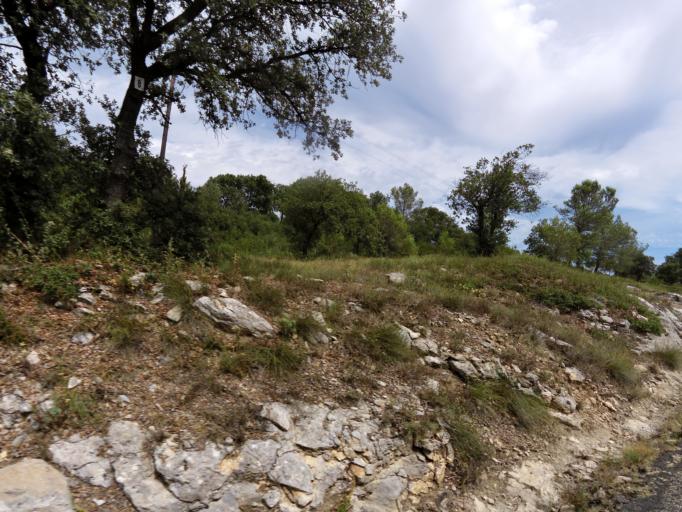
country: FR
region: Languedoc-Roussillon
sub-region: Departement du Gard
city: Congenies
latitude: 43.8109
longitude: 4.1486
